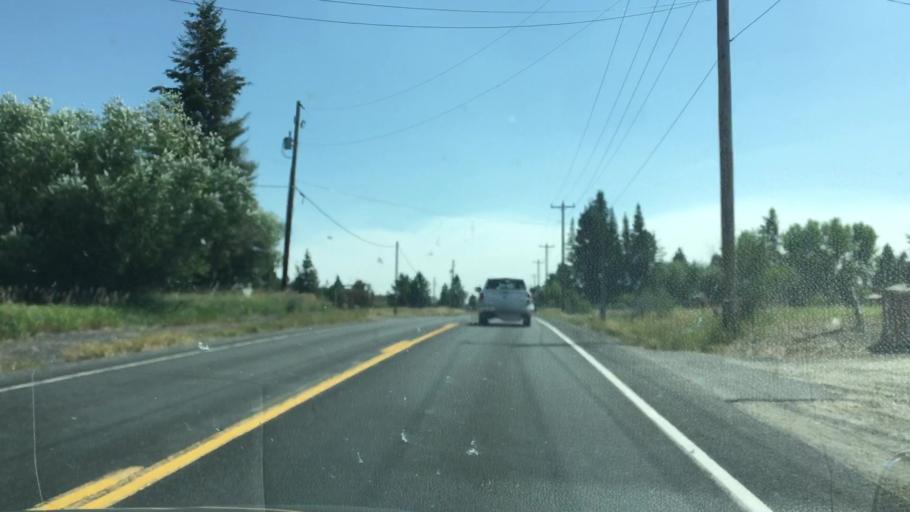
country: US
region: Idaho
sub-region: Valley County
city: McCall
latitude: 44.8722
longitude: -116.0908
